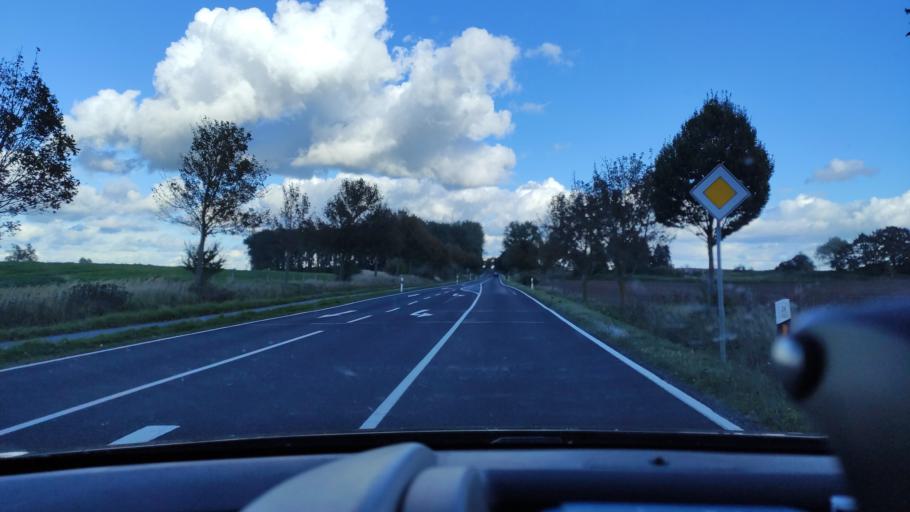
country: DE
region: Mecklenburg-Vorpommern
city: Guestrow
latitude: 53.7571
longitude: 12.1175
